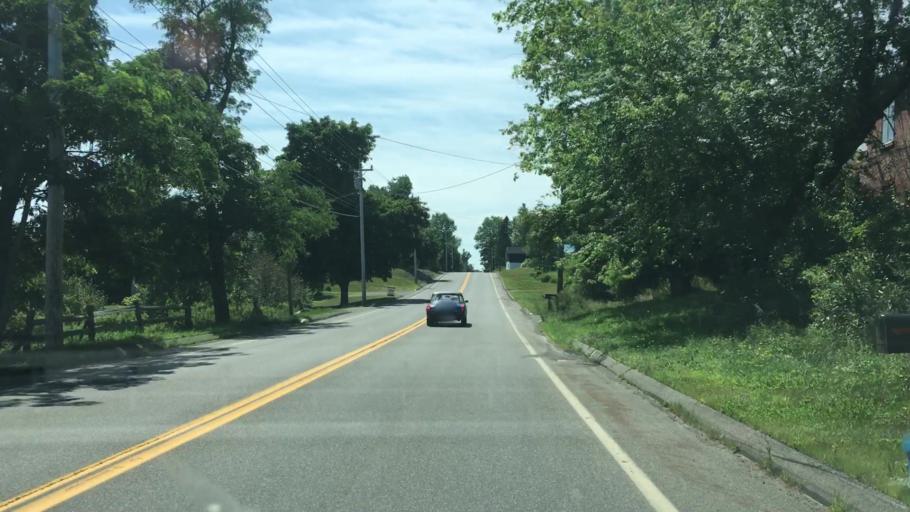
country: CA
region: New Brunswick
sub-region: Charlotte County
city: Saint Andrews
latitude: 45.0811
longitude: -67.1101
